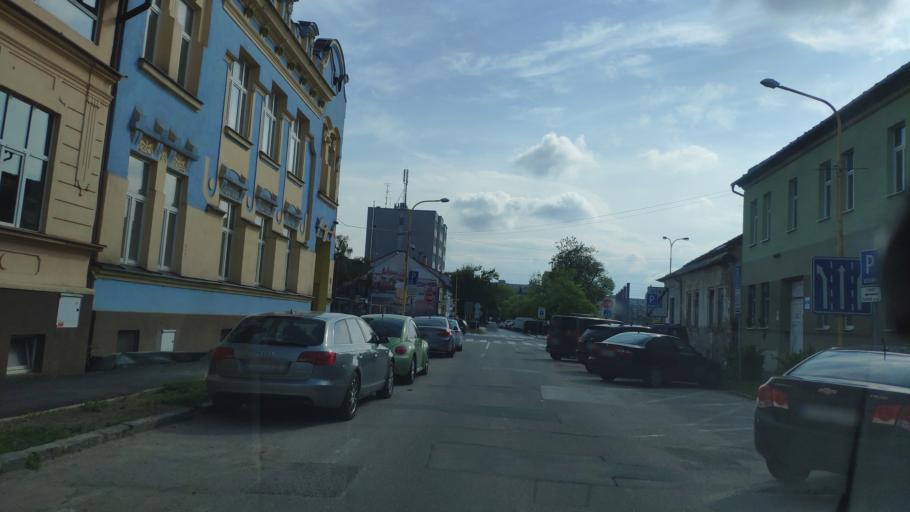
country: SK
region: Kosicky
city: Kosice
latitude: 48.7141
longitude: 21.2536
